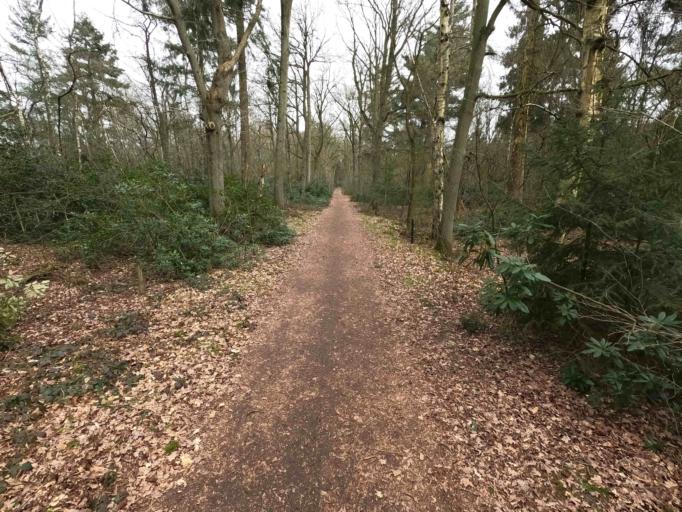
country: BE
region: Flanders
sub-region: Provincie Antwerpen
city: Kalmthout
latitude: 51.3997
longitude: 4.4516
